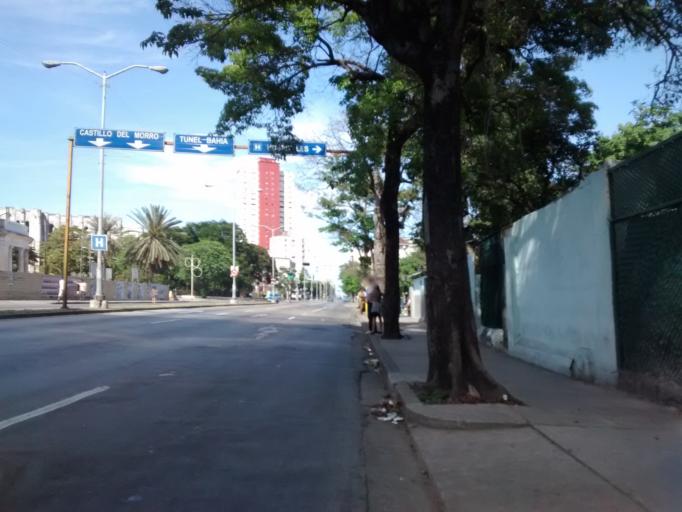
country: CU
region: La Habana
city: Havana
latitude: 23.1409
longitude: -82.3935
